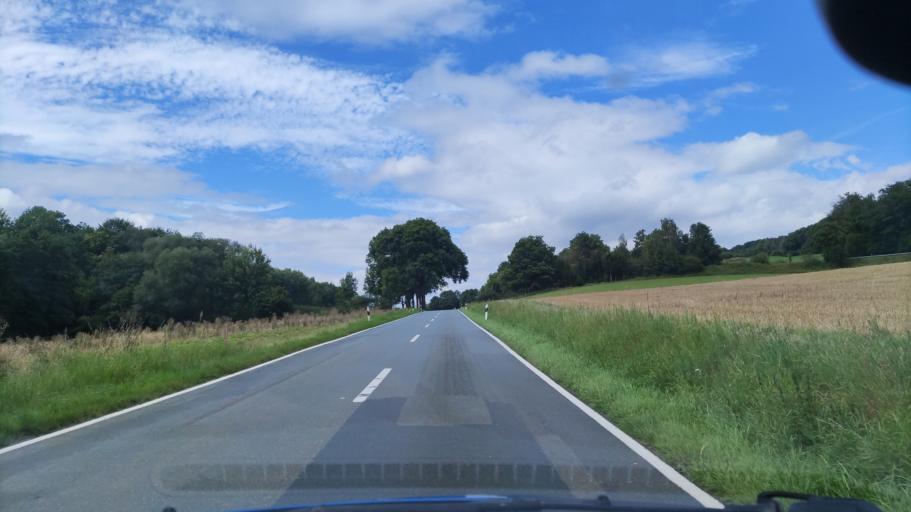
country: DE
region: Lower Saxony
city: Delligsen
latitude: 51.9581
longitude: 9.7842
